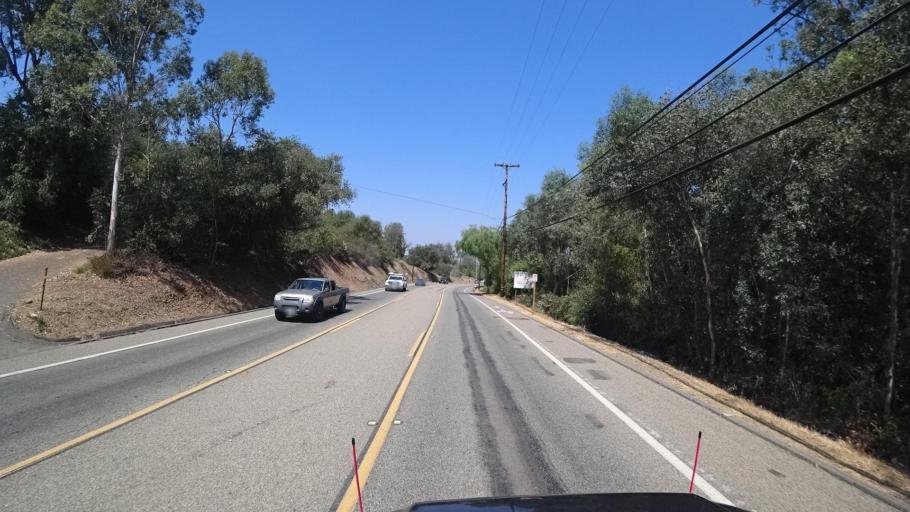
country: US
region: California
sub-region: San Diego County
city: Bonsall
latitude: 33.2532
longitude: -117.2326
